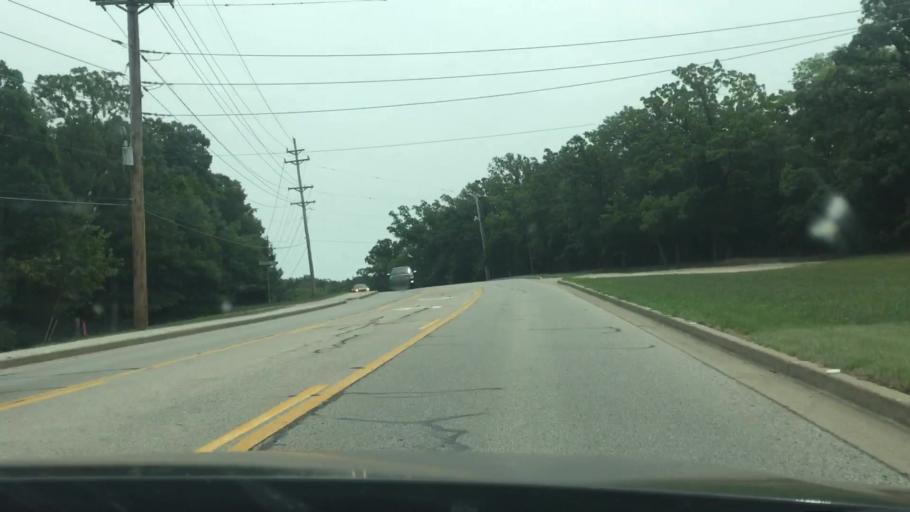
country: US
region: Missouri
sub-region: Camden County
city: Four Seasons
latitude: 38.1917
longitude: -92.7018
